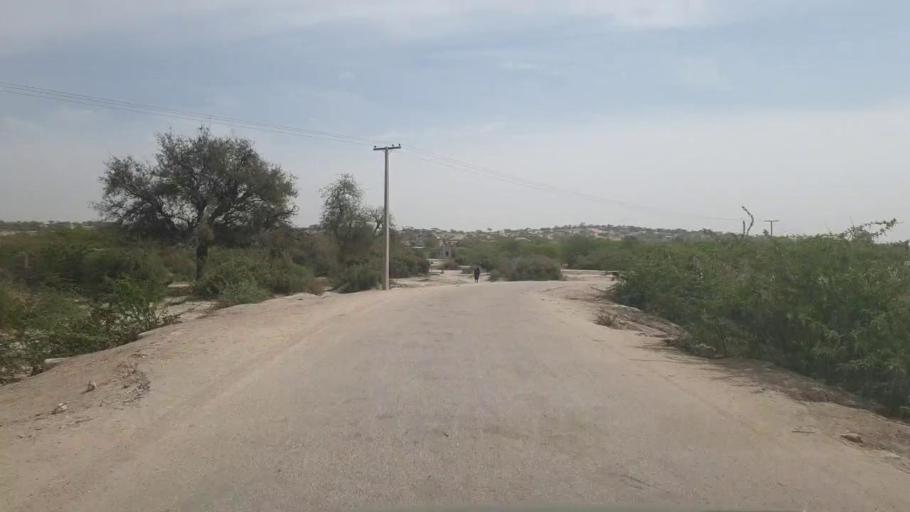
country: PK
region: Sindh
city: Umarkot
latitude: 25.2250
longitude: 69.7132
